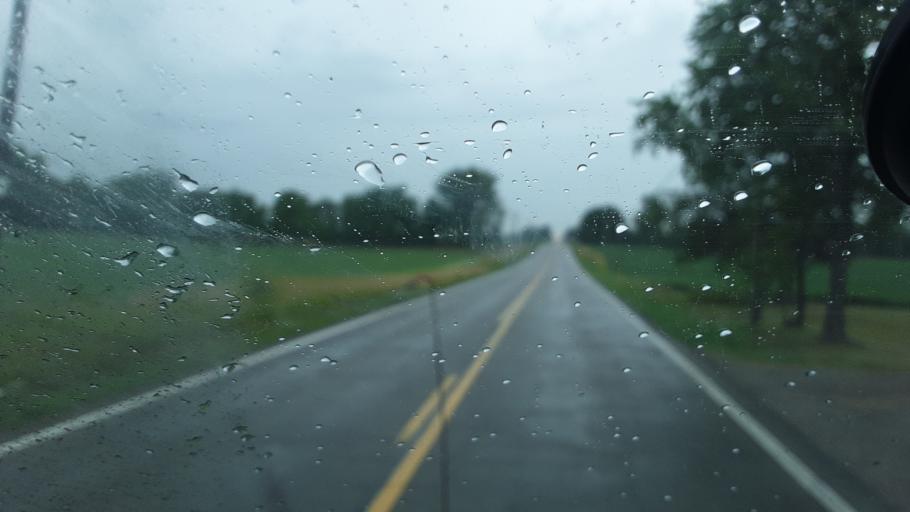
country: US
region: Ohio
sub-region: Williams County
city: Montpelier
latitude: 41.5335
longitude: -84.6130
